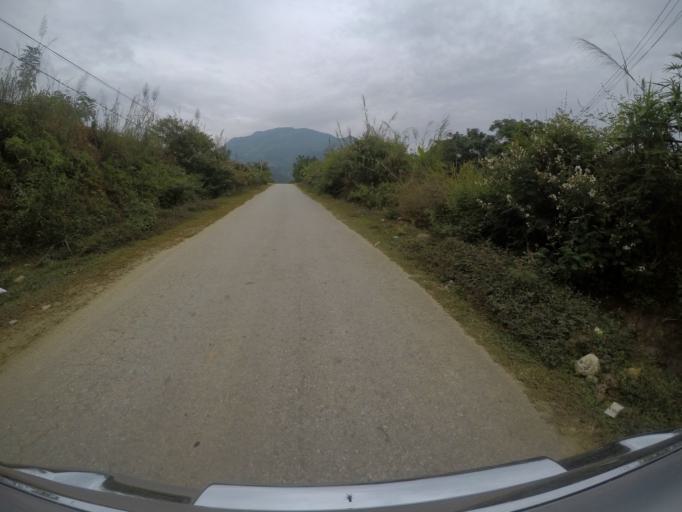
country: VN
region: Yen Bai
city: Son Thinh
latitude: 21.6570
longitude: 104.5010
